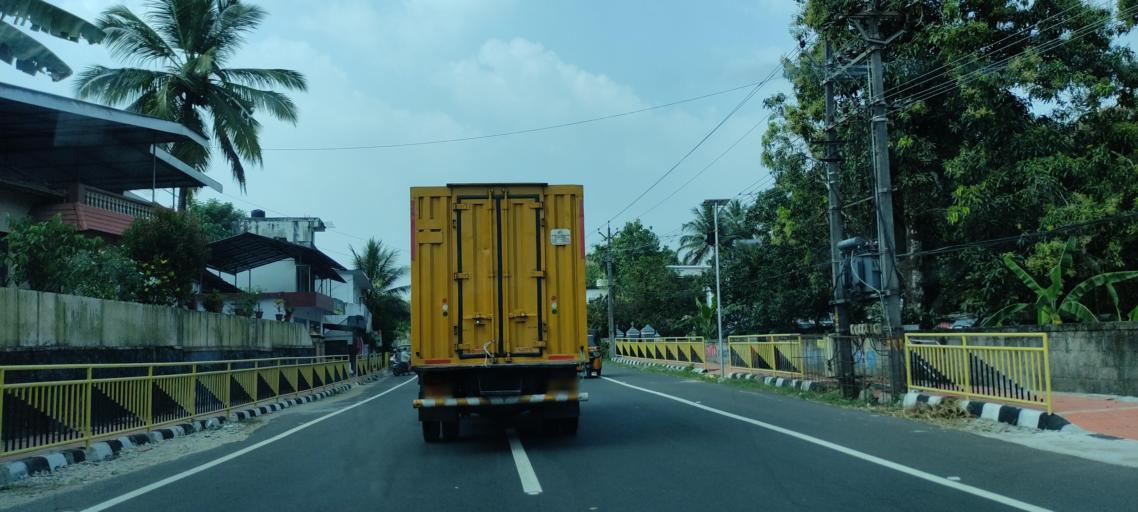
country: IN
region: Kerala
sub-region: Alappuzha
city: Chengannur
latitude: 9.2945
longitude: 76.6429
